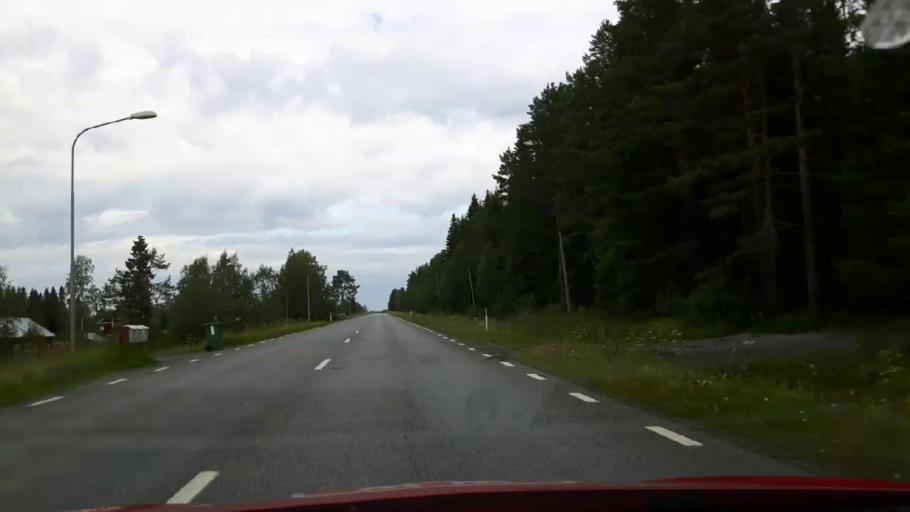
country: SE
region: Jaemtland
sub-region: Stroemsunds Kommun
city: Stroemsund
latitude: 63.5632
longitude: 15.3677
